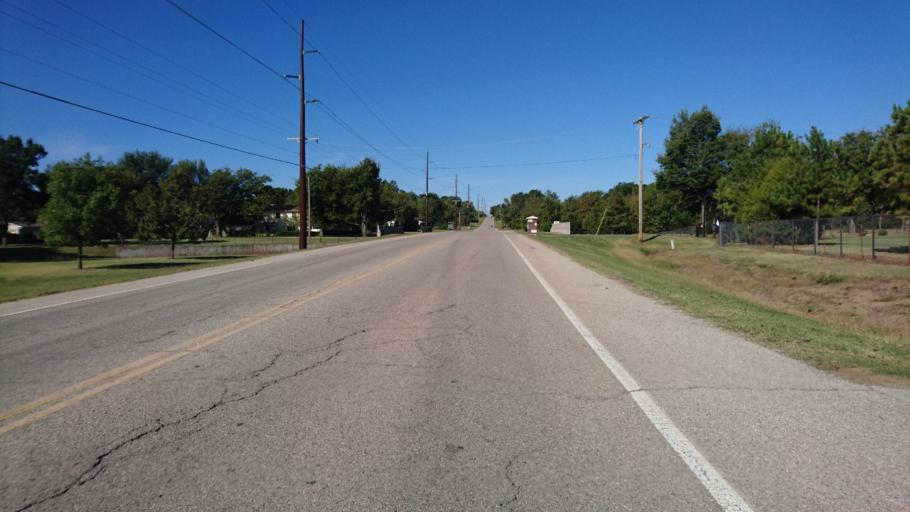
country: US
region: Oklahoma
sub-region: Rogers County
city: Catoosa
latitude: 36.1480
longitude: -95.7851
